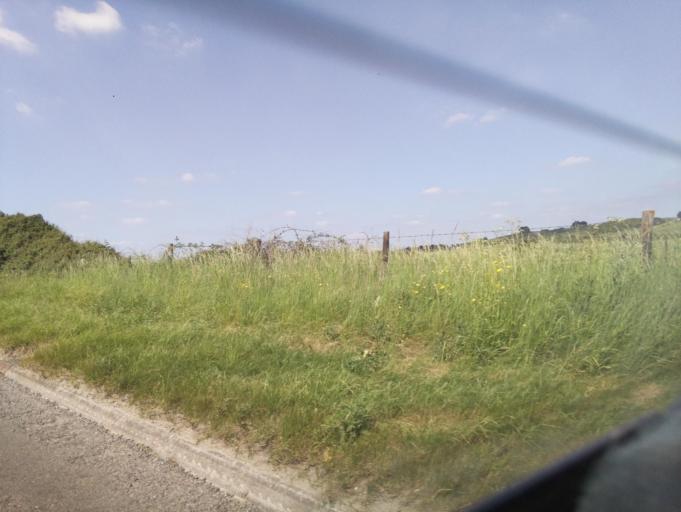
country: GB
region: England
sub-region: Wiltshire
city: Tidworth
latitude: 51.2504
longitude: -1.6659
